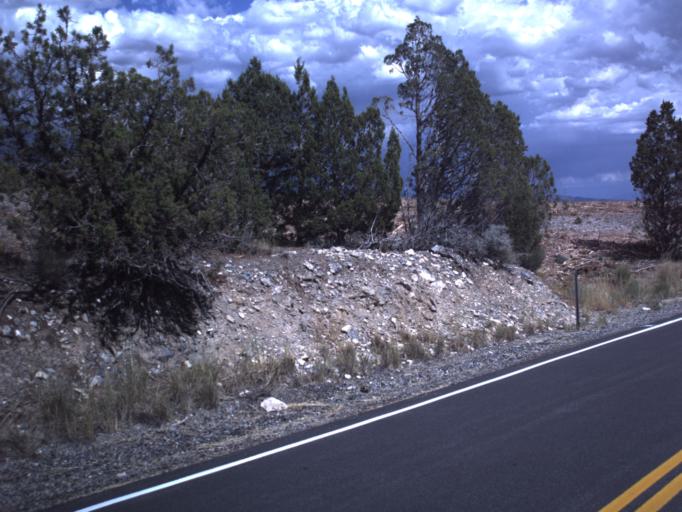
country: US
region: Utah
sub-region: Tooele County
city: Grantsville
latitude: 40.3363
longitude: -112.5302
